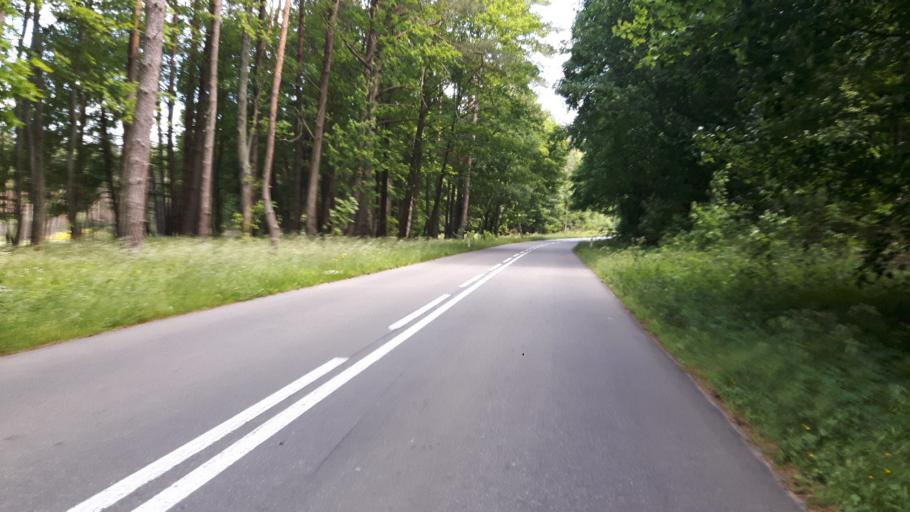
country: PL
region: Pomeranian Voivodeship
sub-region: Powiat leborski
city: Leba
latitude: 54.7450
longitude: 17.7166
